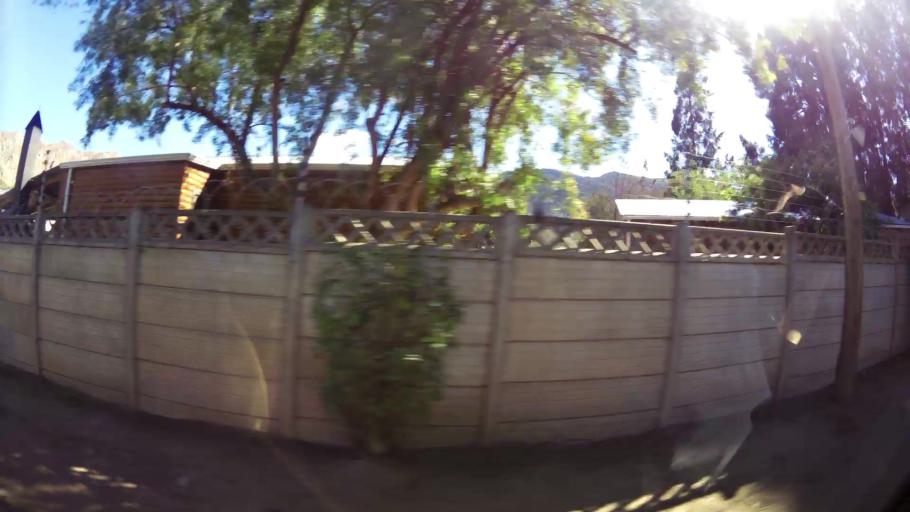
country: ZA
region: Western Cape
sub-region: Cape Winelands District Municipality
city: Ashton
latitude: -33.7869
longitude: 20.1137
